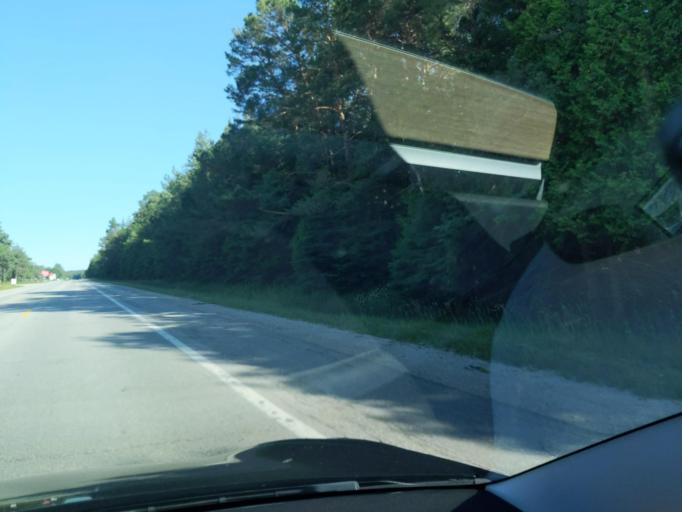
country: US
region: Michigan
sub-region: Mackinac County
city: Saint Ignace
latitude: 45.7581
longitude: -84.7038
